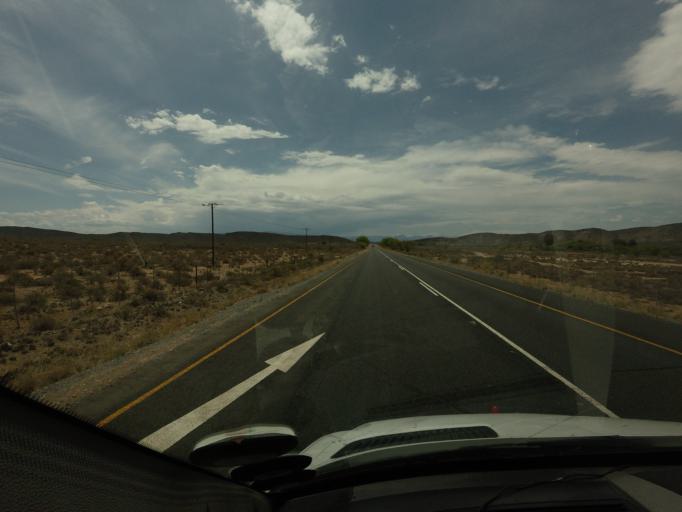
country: ZA
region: Western Cape
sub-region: Eden District Municipality
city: Ladismith
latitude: -33.7786
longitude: 20.9324
